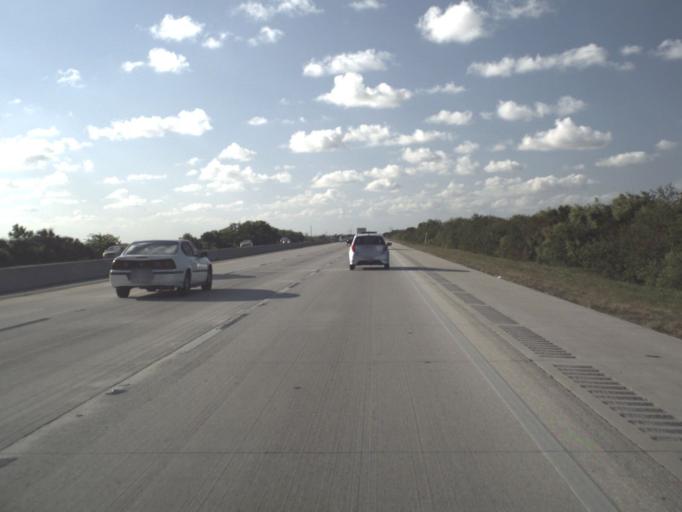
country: US
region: Florida
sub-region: Brevard County
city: Cocoa West
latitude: 28.3063
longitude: -80.7592
